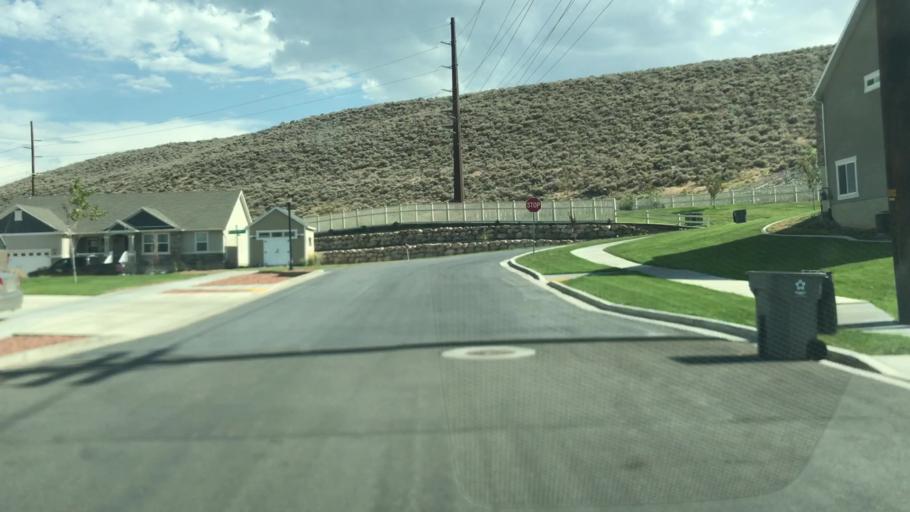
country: US
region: Utah
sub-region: Utah County
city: Saratoga Springs
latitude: 40.3330
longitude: -111.9157
